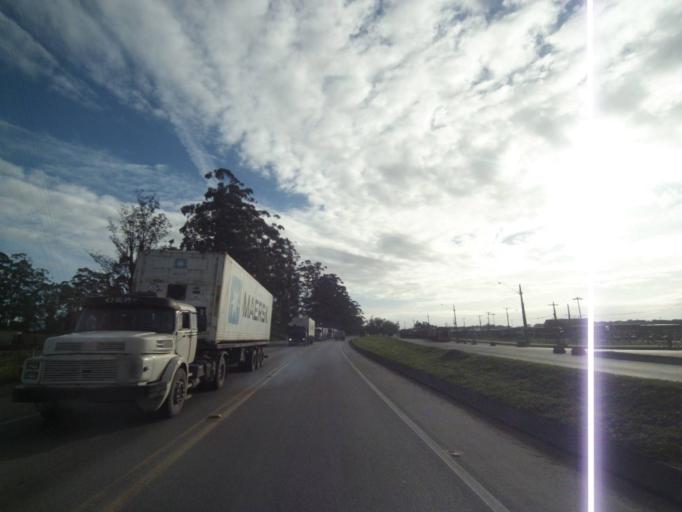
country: BR
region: Parana
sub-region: Paranagua
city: Paranagua
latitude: -25.5401
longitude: -48.5585
